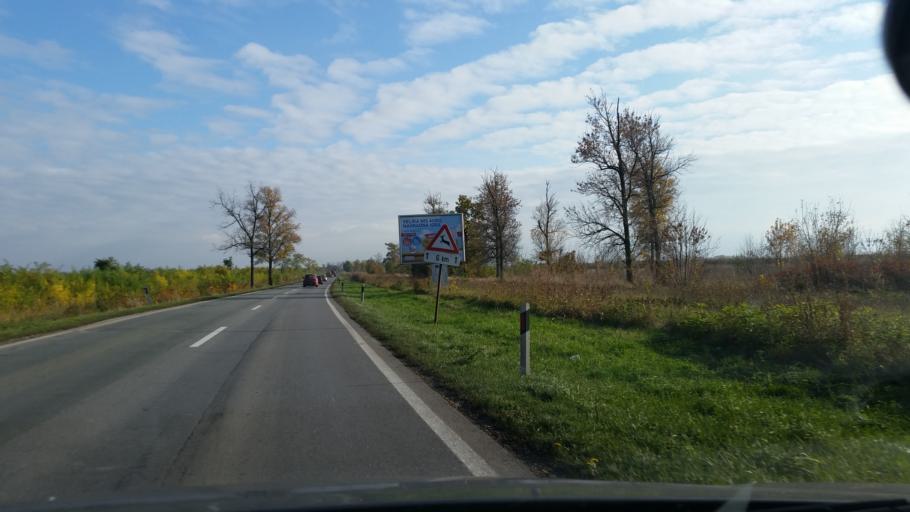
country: RS
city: Ecka
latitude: 45.3470
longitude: 20.4254
